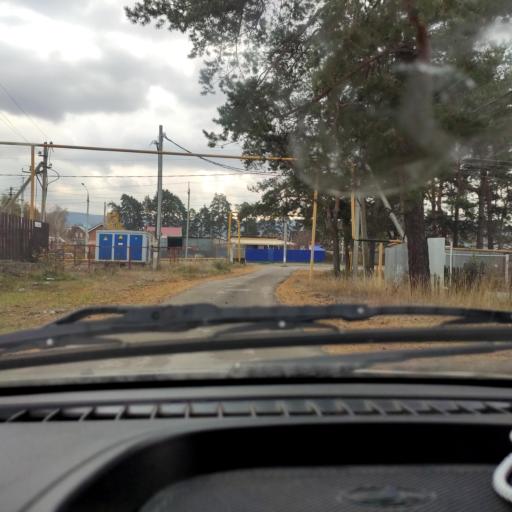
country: RU
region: Samara
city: Zhigulevsk
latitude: 53.4662
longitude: 49.6057
